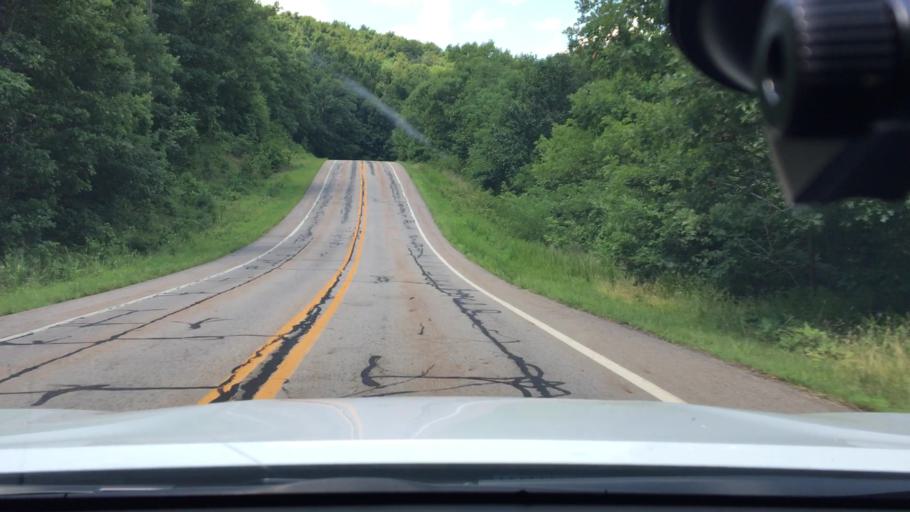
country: US
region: Arkansas
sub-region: Logan County
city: Paris
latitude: 35.1737
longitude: -93.6251
